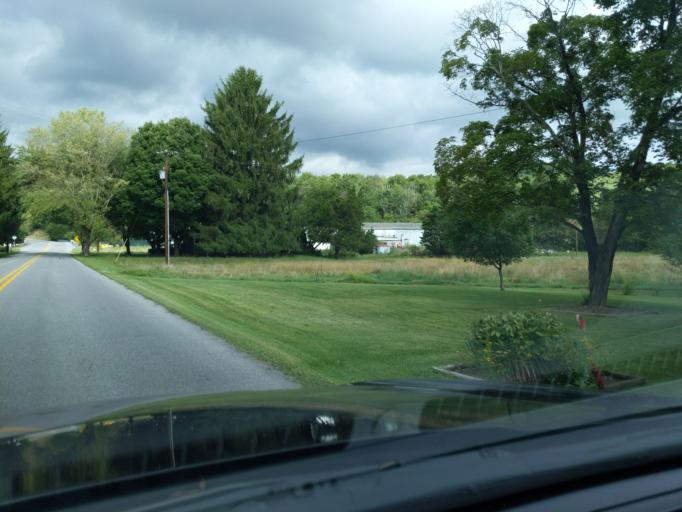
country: US
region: Pennsylvania
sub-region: Blair County
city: Claysburg
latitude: 40.3534
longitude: -78.4453
